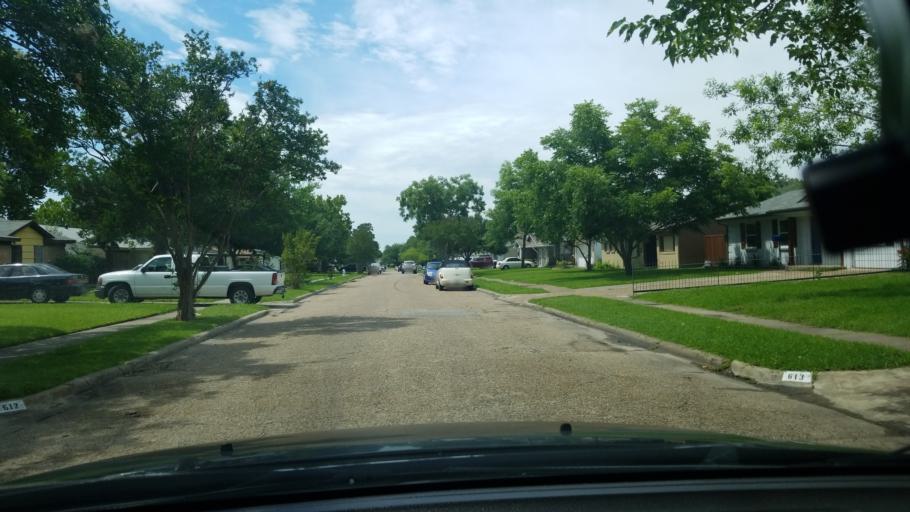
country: US
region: Texas
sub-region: Dallas County
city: Mesquite
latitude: 32.7598
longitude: -96.5811
